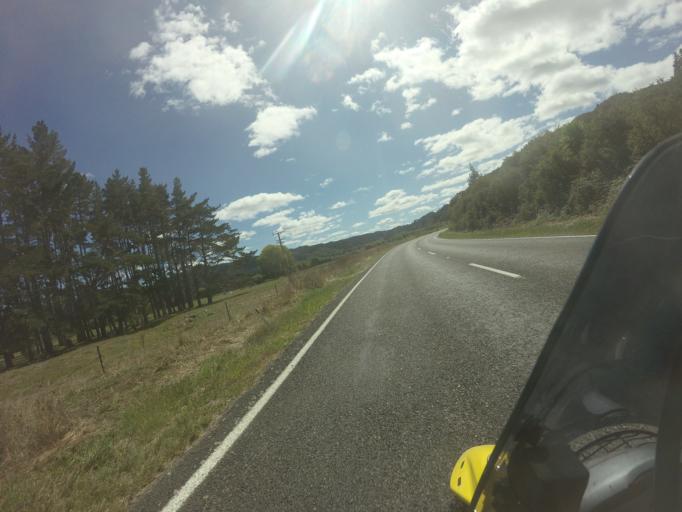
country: NZ
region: Bay of Plenty
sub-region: Kawerau District
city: Kawerau
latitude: -38.1977
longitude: 176.8421
